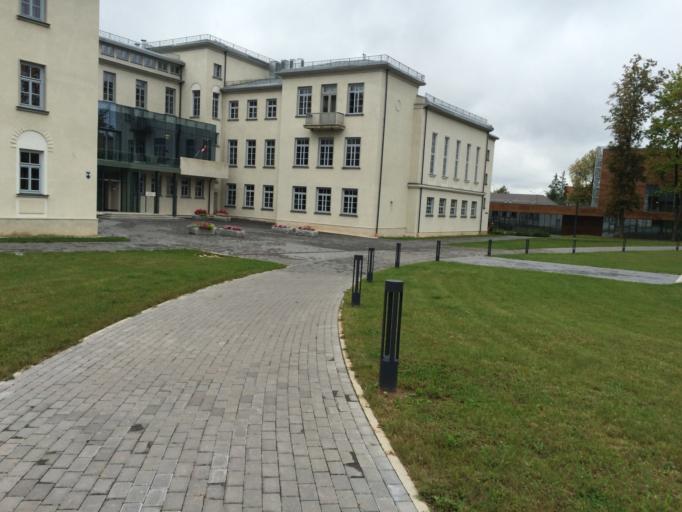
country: LV
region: Rezekne
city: Rezekne
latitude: 56.5124
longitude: 27.3335
